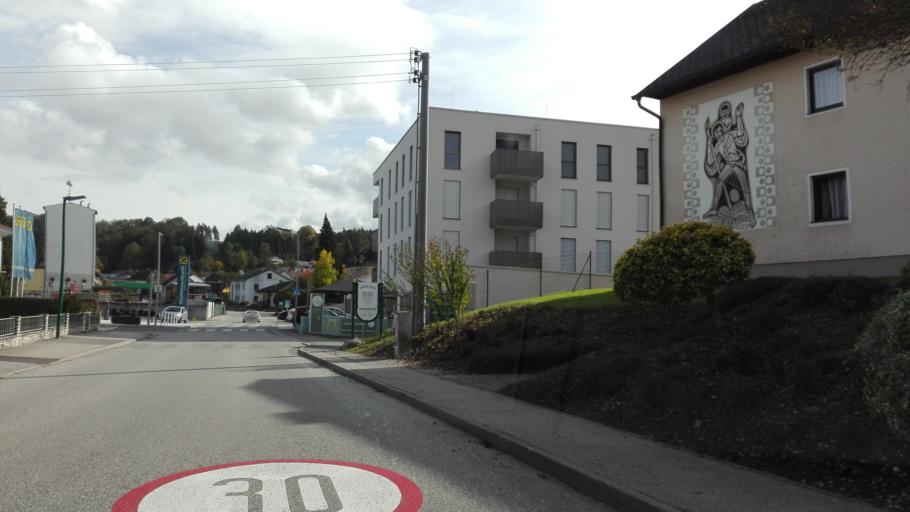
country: AT
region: Upper Austria
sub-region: Wels-Land
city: Marchtrenk
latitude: 48.1634
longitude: 14.1194
